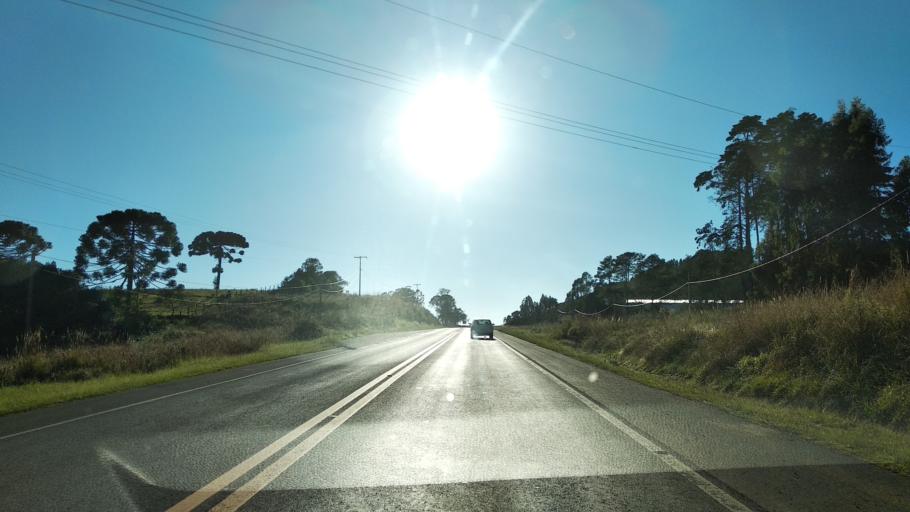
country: BR
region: Santa Catarina
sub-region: Lages
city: Lages
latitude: -27.7943
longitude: -50.3798
